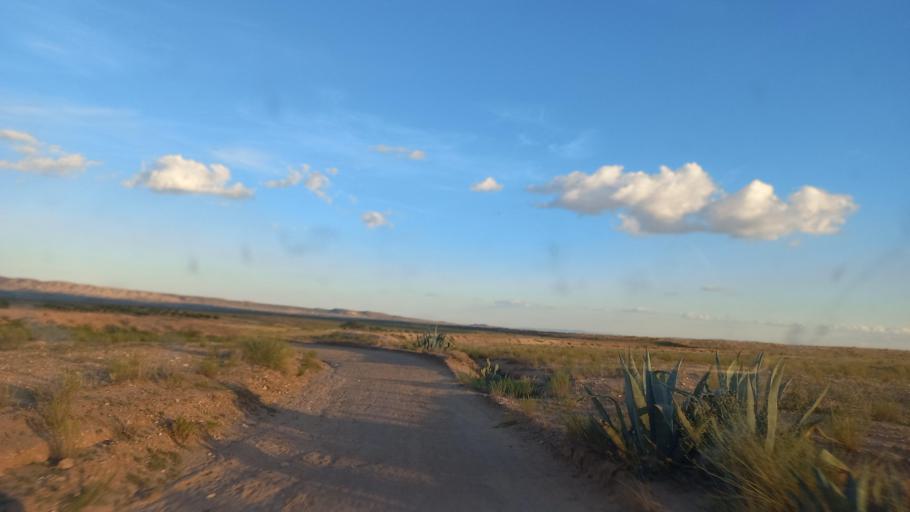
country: TN
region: Al Qasrayn
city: Sbiba
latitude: 35.3496
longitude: 9.0232
